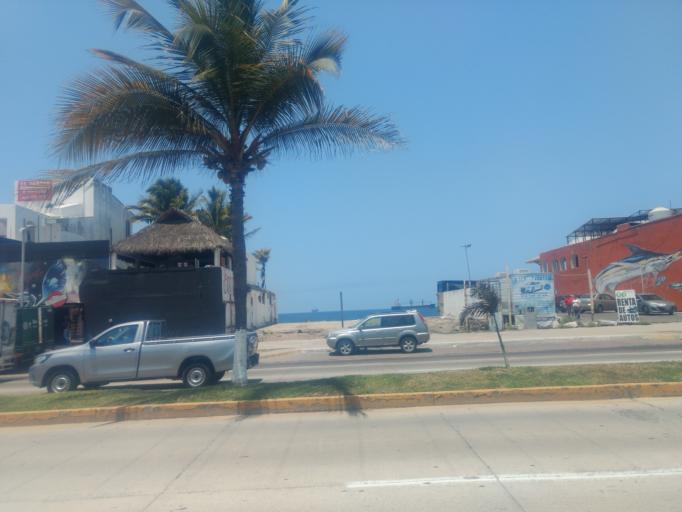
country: MX
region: Colima
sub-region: Manzanillo
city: Manzanillo
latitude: 19.0922
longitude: -104.3157
